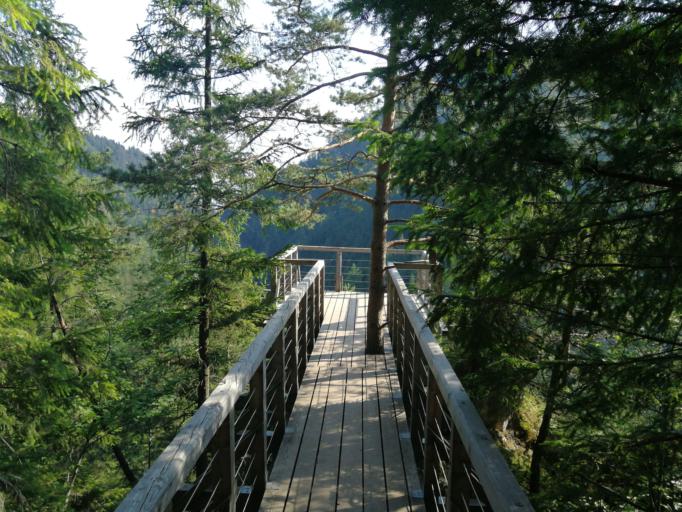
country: SK
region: Zilinsky
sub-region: Okres Liptovsky Mikulas
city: Liptovsky Mikulas
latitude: 49.1944
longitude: 19.5447
